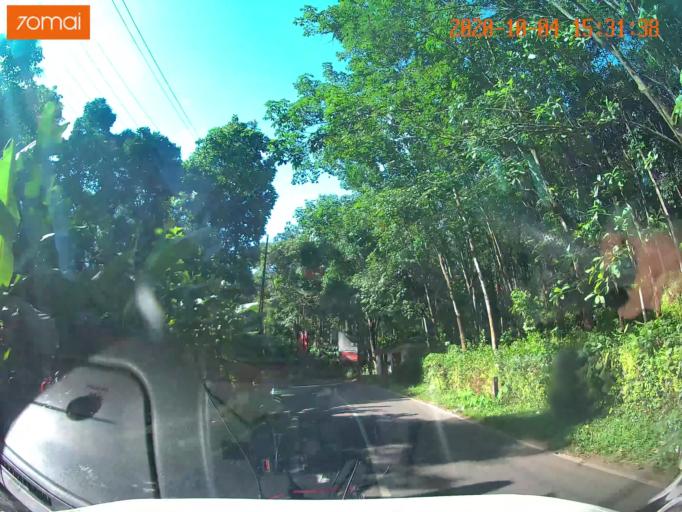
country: IN
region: Kerala
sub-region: Kottayam
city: Palackattumala
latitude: 9.7309
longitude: 76.6382
